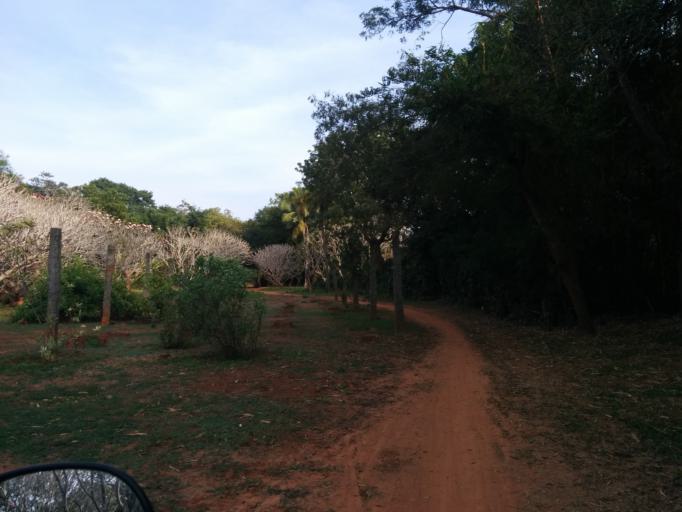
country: IN
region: Tamil Nadu
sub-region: Villupuram
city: Auroville
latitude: 12.0084
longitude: 79.8059
